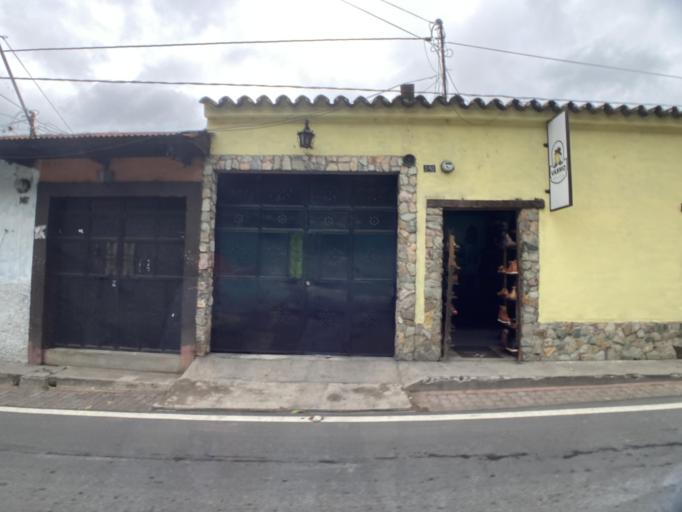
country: GT
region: Sacatepequez
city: Pastores
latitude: 14.5943
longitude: -90.7537
